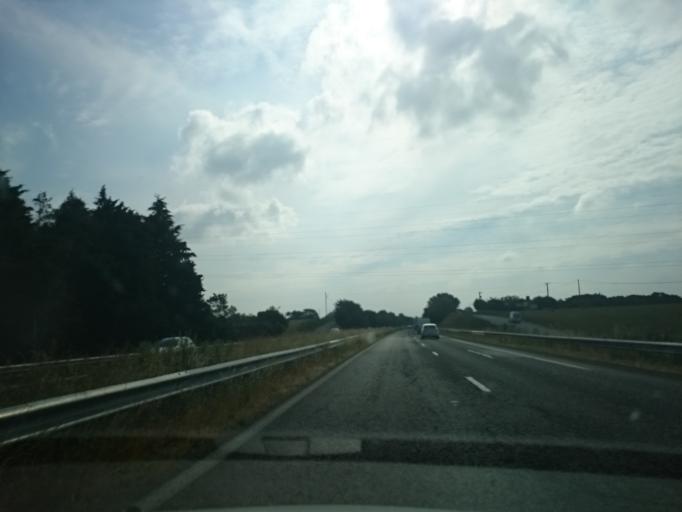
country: FR
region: Brittany
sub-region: Departement du Morbihan
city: Ploeren
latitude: 47.6612
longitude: -2.8295
